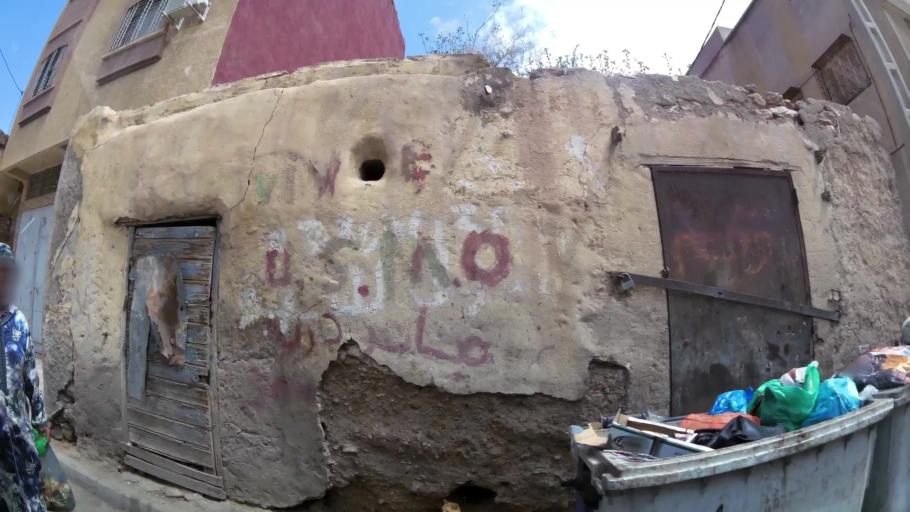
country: MA
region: Oriental
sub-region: Oujda-Angad
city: Oujda
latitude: 34.6807
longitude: -1.9016
